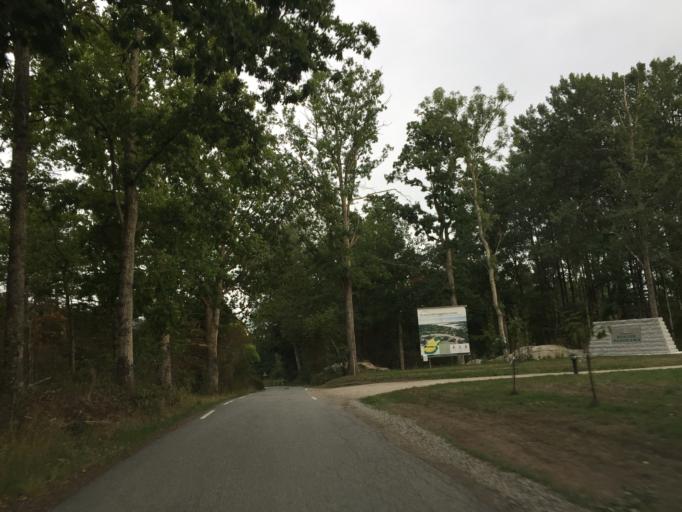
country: NO
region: Ostfold
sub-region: Hvaler
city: Skjaerhalden
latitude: 59.0572
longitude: 11.0098
